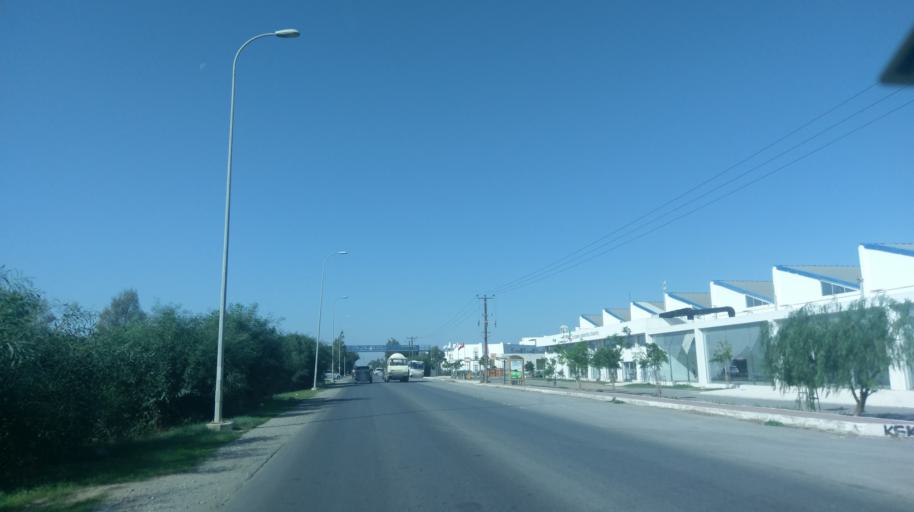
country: CY
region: Ammochostos
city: Famagusta
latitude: 35.1425
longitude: 33.9016
